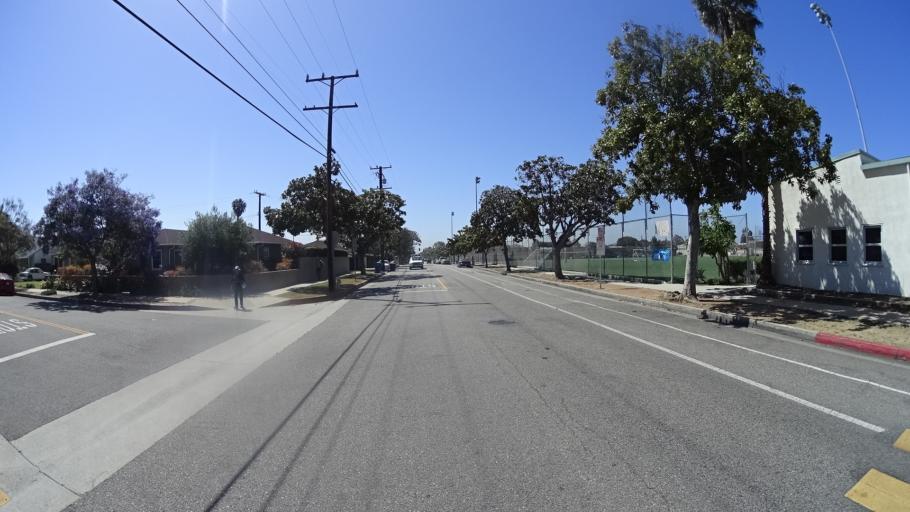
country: US
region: California
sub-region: Los Angeles County
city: Santa Monica
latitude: 34.0139
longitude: -118.4684
